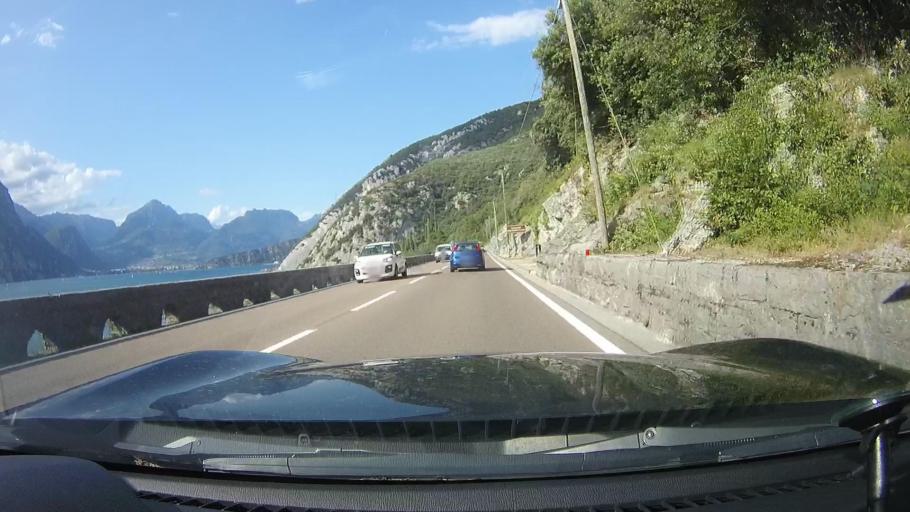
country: IT
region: Trentino-Alto Adige
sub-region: Provincia di Trento
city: Torbole sul Garda
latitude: 45.8415
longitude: 10.8618
